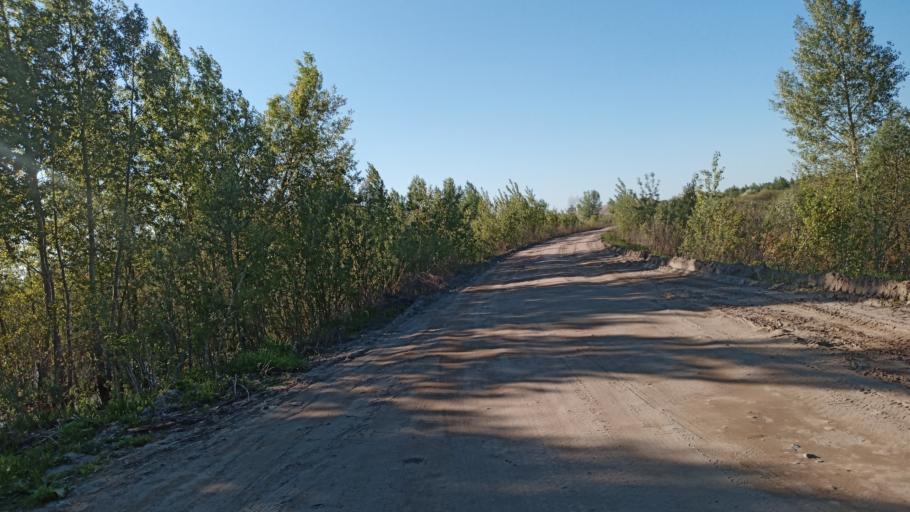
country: RU
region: Altai Krai
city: Zaton
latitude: 53.3067
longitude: 83.8248
